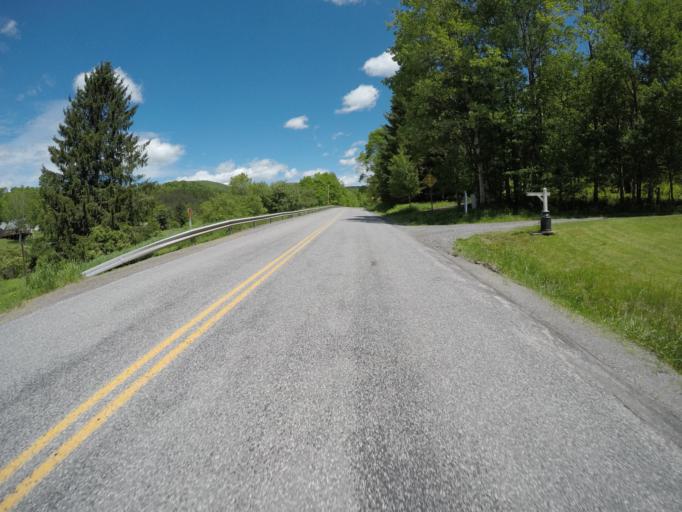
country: US
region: New York
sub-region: Delaware County
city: Stamford
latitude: 42.2282
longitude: -74.5632
